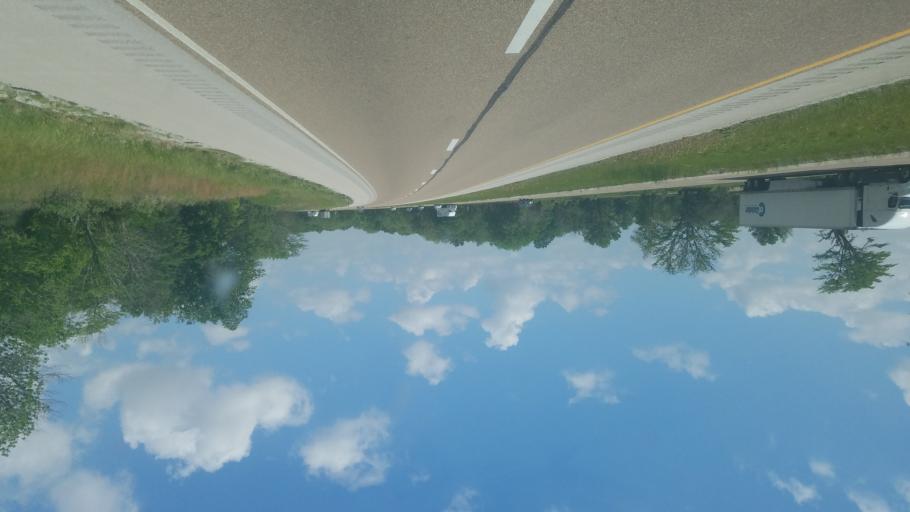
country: US
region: Illinois
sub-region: Clark County
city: Casey
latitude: 39.2847
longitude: -88.0497
